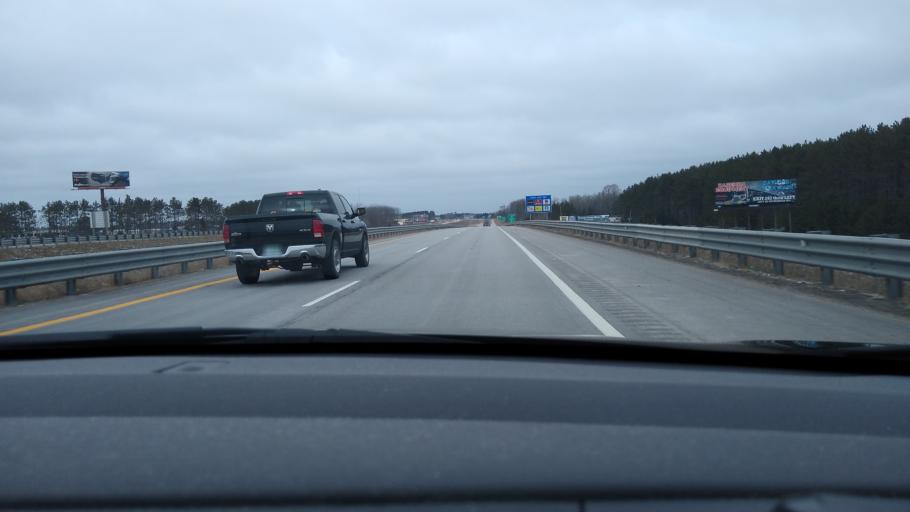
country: US
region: Michigan
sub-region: Otsego County
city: Gaylord
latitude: 45.0038
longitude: -84.6854
